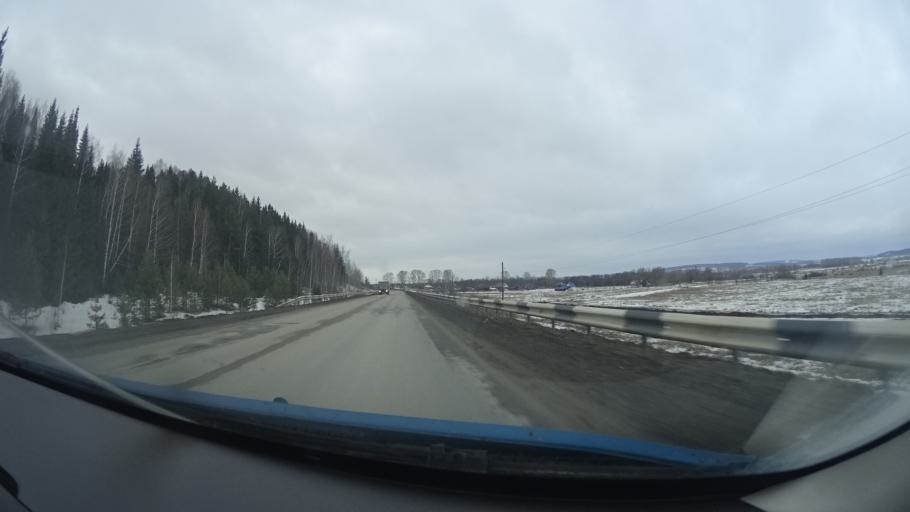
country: RU
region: Perm
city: Osa
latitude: 57.2084
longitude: 55.5891
